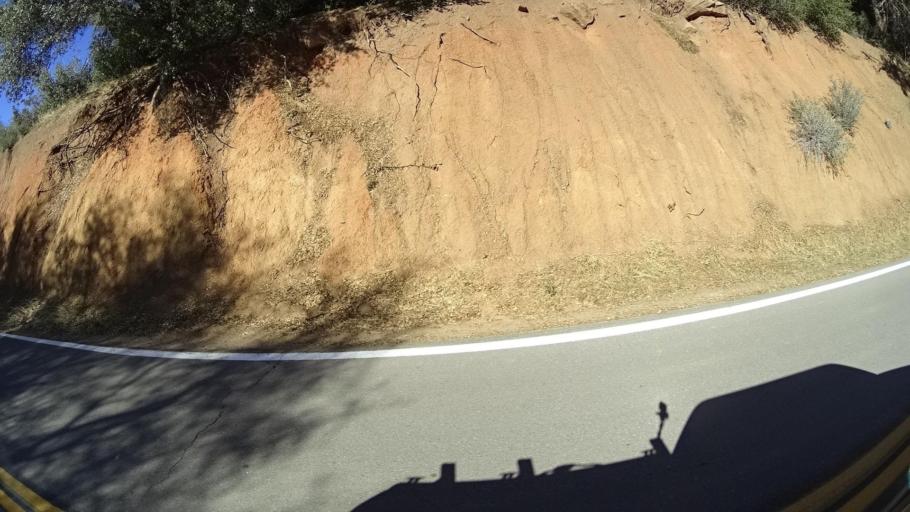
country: US
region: California
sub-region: Kern County
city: Alta Sierra
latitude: 35.7471
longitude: -118.5893
